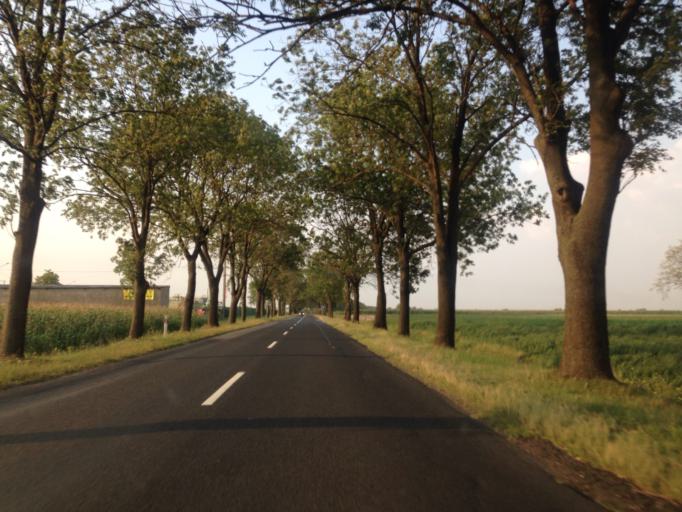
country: PL
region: Kujawsko-Pomorskie
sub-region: Powiat lipnowski
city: Lipno
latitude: 52.8801
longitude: 19.1995
